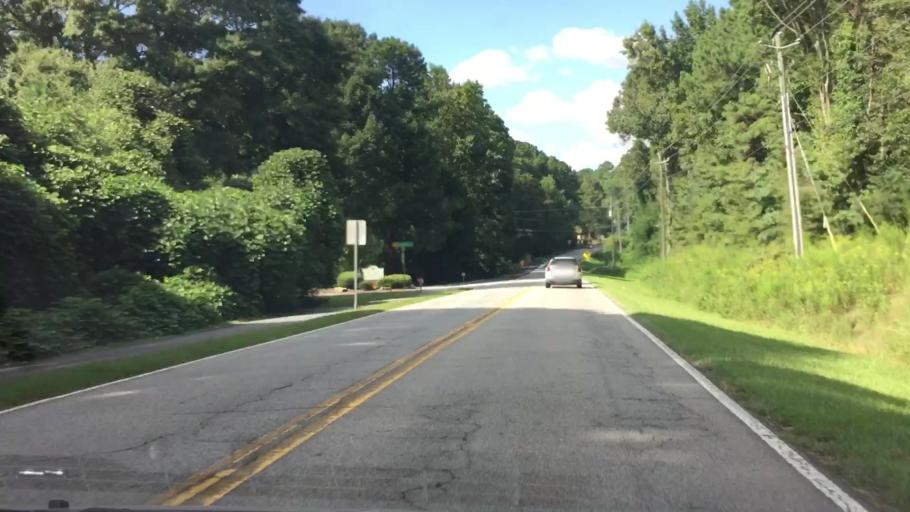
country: US
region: Georgia
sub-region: Fayette County
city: Fayetteville
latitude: 33.4331
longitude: -84.4601
